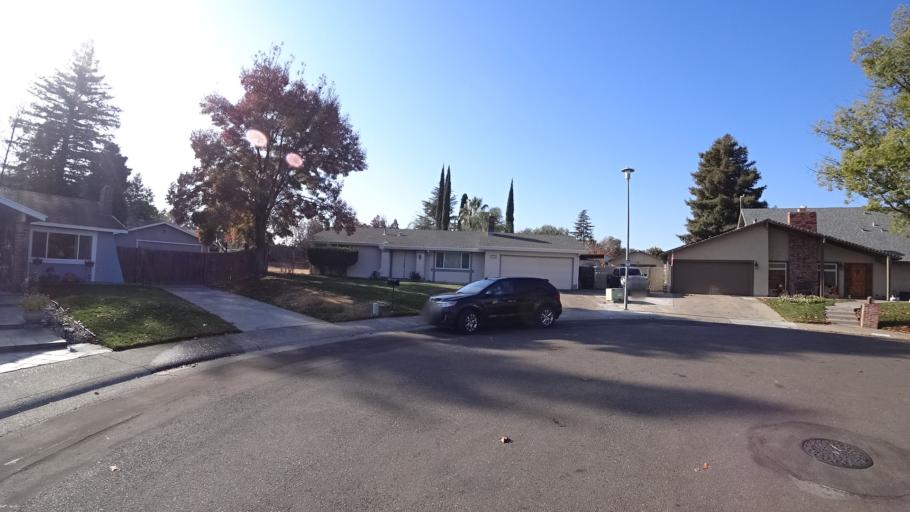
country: US
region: California
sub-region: Sacramento County
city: Orangevale
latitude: 38.6970
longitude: -121.2500
